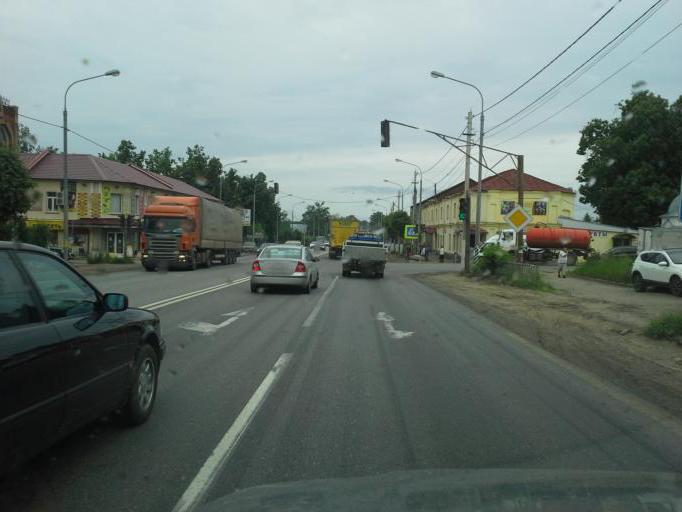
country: RU
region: Vladimir
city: Pokrov
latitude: 55.9185
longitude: 39.1823
